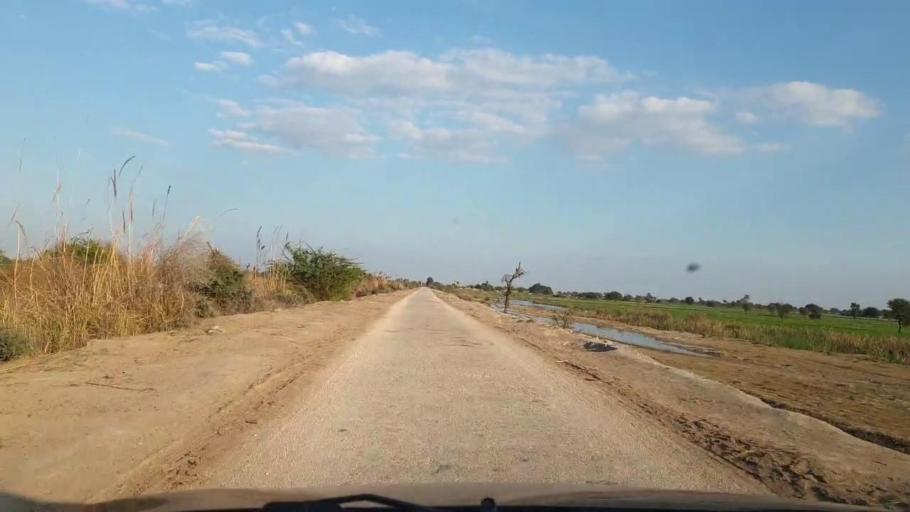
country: PK
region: Sindh
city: Sinjhoro
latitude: 25.9938
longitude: 68.7585
